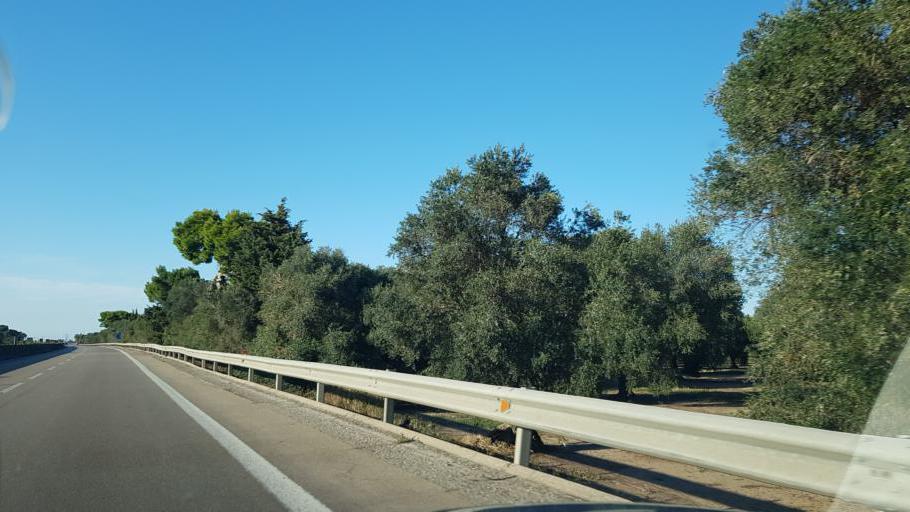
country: IT
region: Apulia
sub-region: Provincia di Brindisi
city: La Rosa
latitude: 40.5775
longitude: 17.9801
